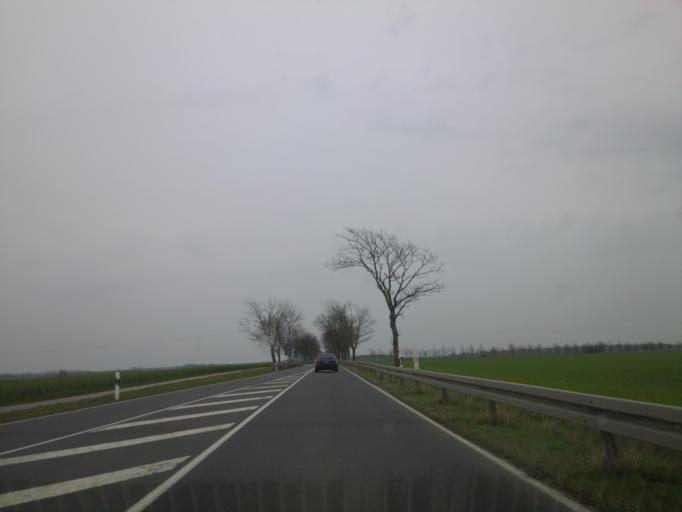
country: DE
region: Mecklenburg-Vorpommern
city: Barth
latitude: 54.3275
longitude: 12.7208
